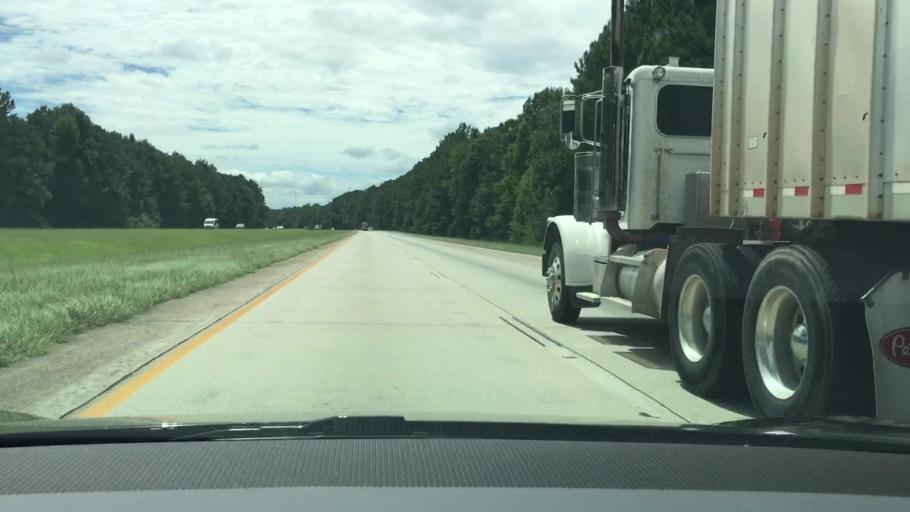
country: US
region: Georgia
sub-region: Troup County
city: Hogansville
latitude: 33.1129
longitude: -84.9032
